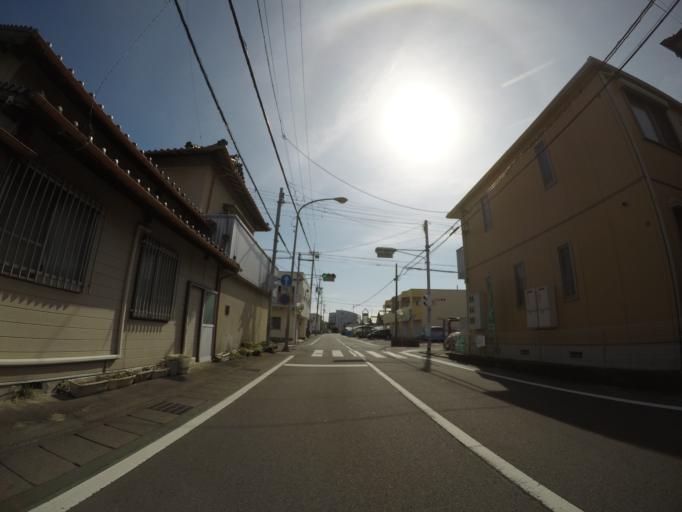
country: JP
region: Shizuoka
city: Shizuoka-shi
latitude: 34.9342
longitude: 138.3772
